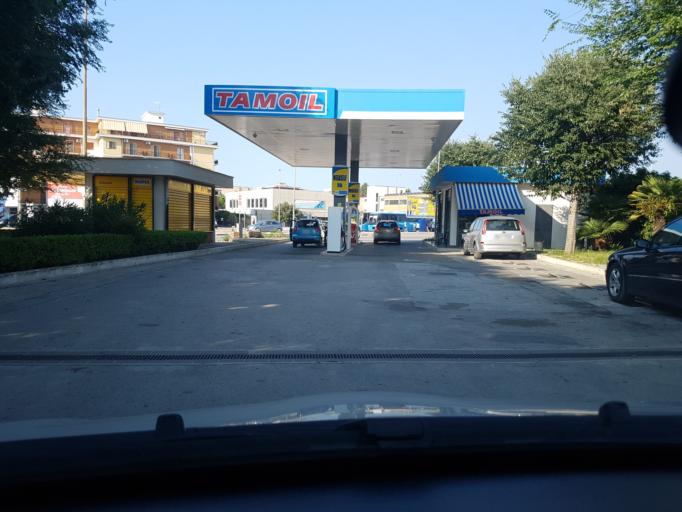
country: IT
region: Apulia
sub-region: Provincia di Foggia
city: Cerignola
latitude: 41.2598
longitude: 15.9074
